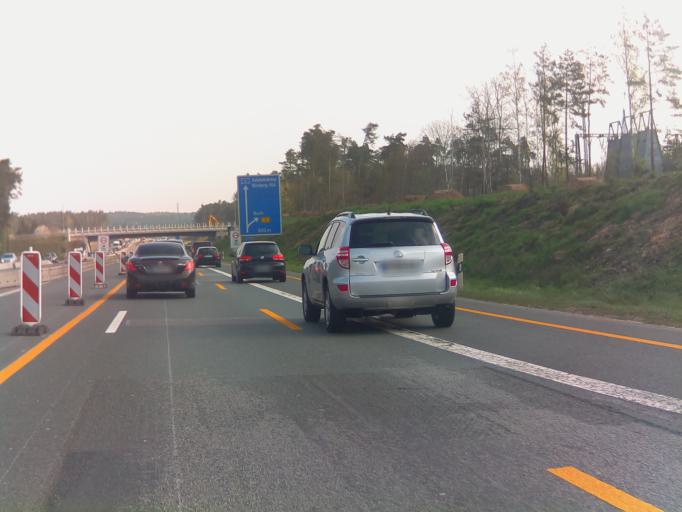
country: DE
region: Bavaria
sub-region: Regierungsbezirk Mittelfranken
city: Schwabach
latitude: 49.3245
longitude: 11.0494
